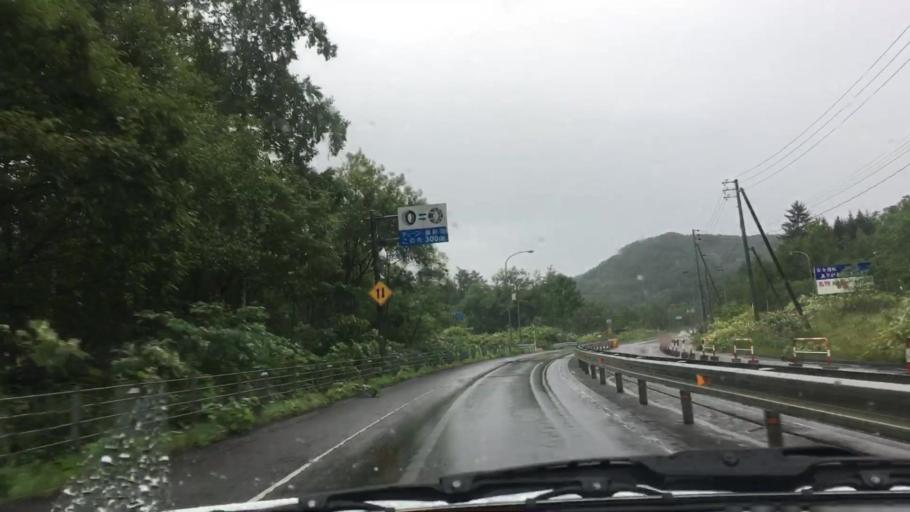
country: JP
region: Hokkaido
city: Niseko Town
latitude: 42.8311
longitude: 141.0092
